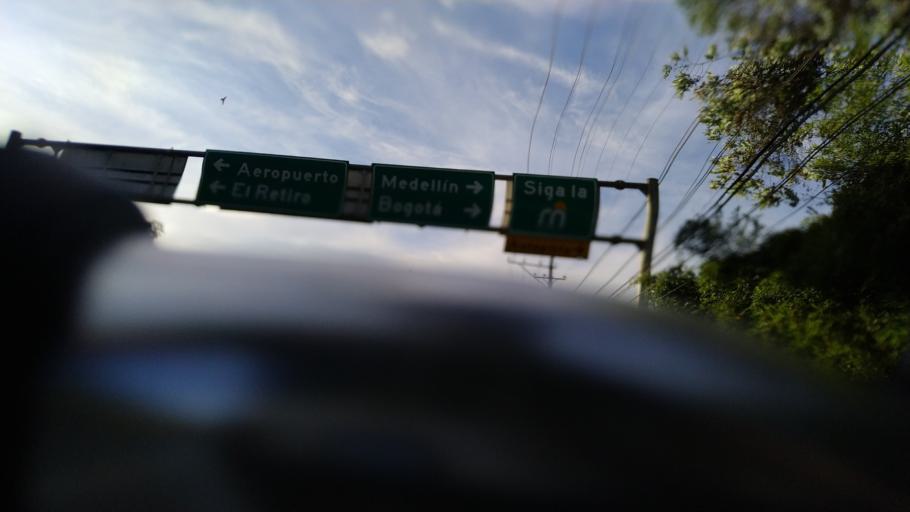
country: CO
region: Antioquia
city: Rionegro
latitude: 6.1388
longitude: -75.3783
